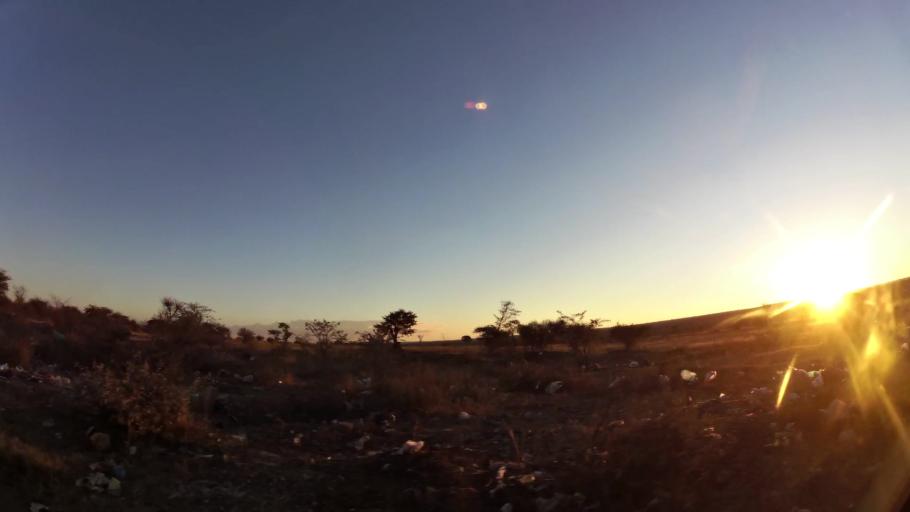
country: ZA
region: Limpopo
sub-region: Capricorn District Municipality
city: Polokwane
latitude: -23.8562
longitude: 29.3619
